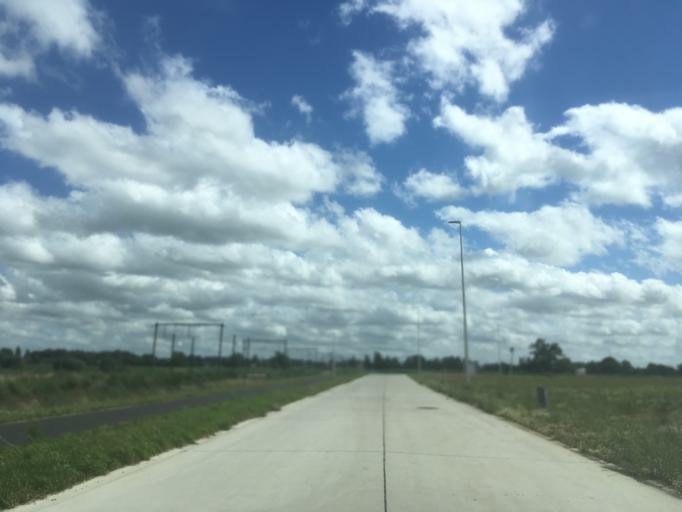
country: BE
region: Flanders
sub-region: Provincie West-Vlaanderen
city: Torhout
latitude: 51.0468
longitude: 3.1104
